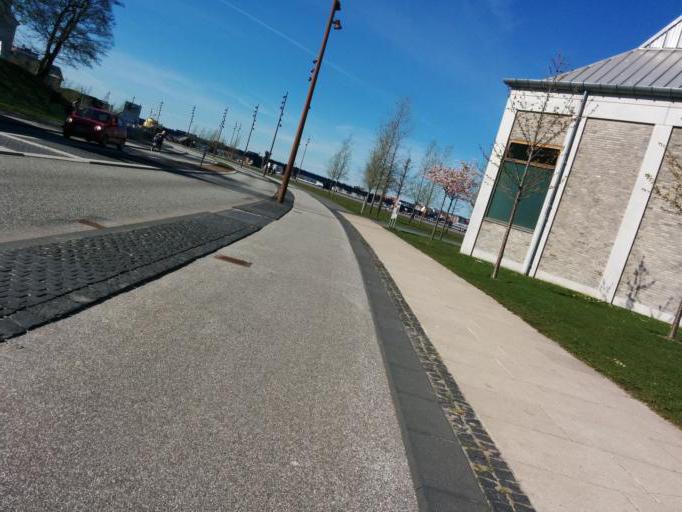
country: DK
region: North Denmark
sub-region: Alborg Kommune
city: Aalborg
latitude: 57.0491
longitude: 9.9260
